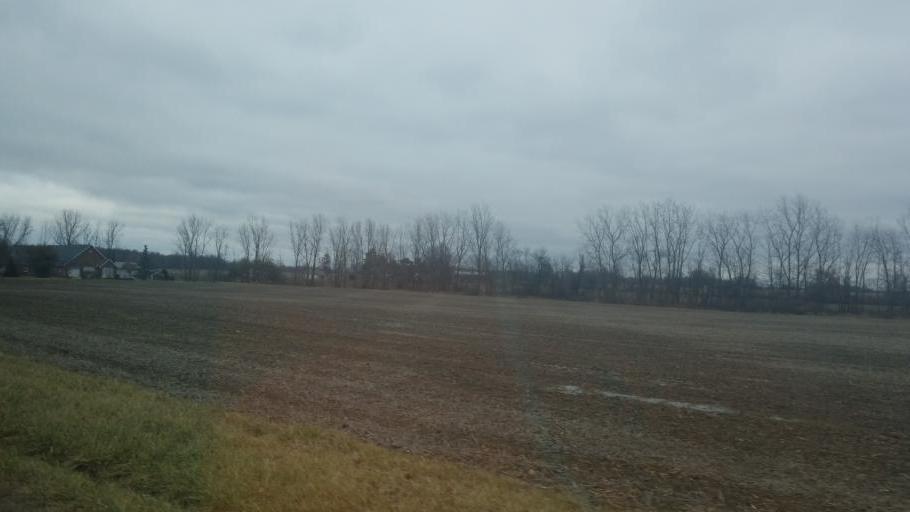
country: US
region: Ohio
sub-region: Crawford County
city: Crestline
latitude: 40.7960
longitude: -82.7169
